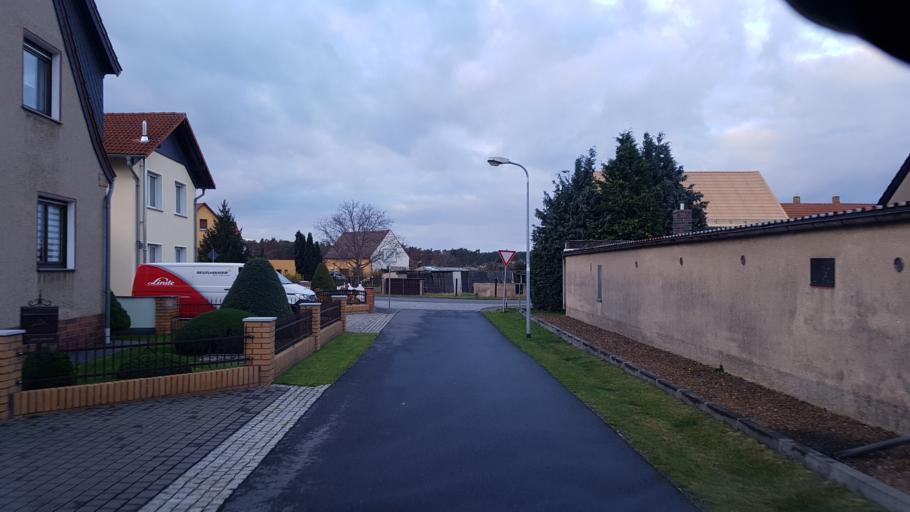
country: DE
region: Brandenburg
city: Lindenau
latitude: 51.4152
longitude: 13.7676
